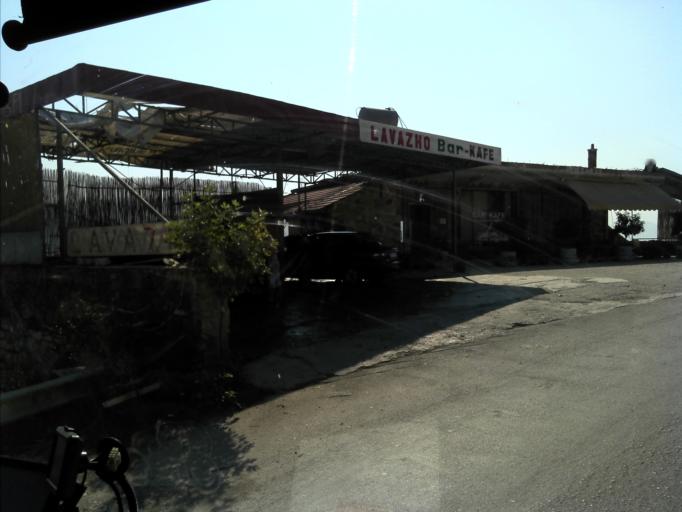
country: AL
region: Vlore
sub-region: Rrethi i Sarandes
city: Sarande
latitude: 39.8781
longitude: 20.0327
